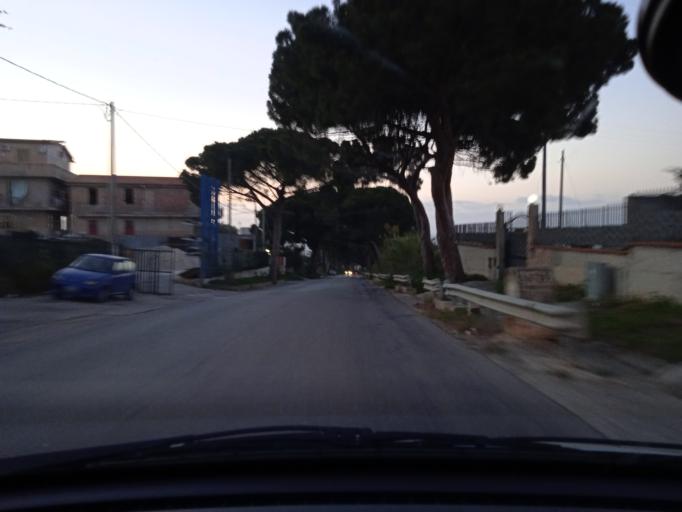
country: IT
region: Sicily
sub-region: Palermo
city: Portella di Mare
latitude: 38.0626
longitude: 13.4600
